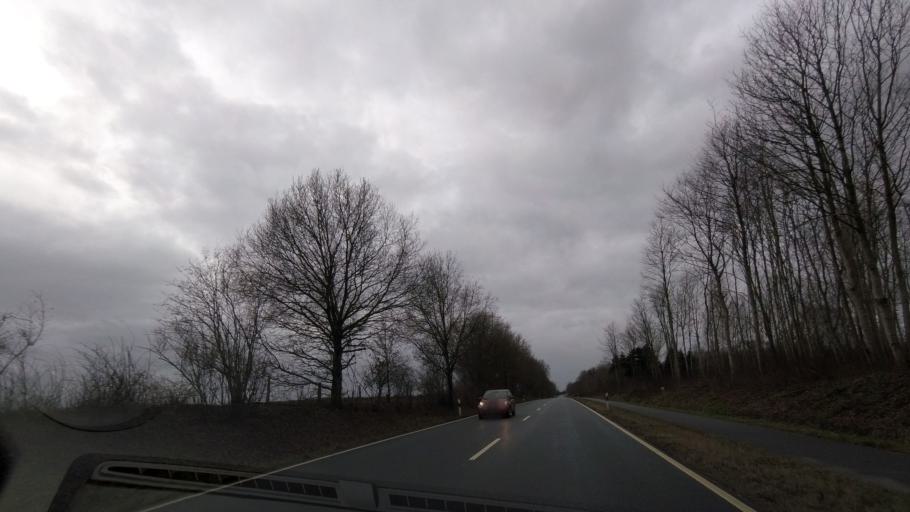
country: DE
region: Schleswig-Holstein
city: Schaalby
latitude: 54.5535
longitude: 9.6128
